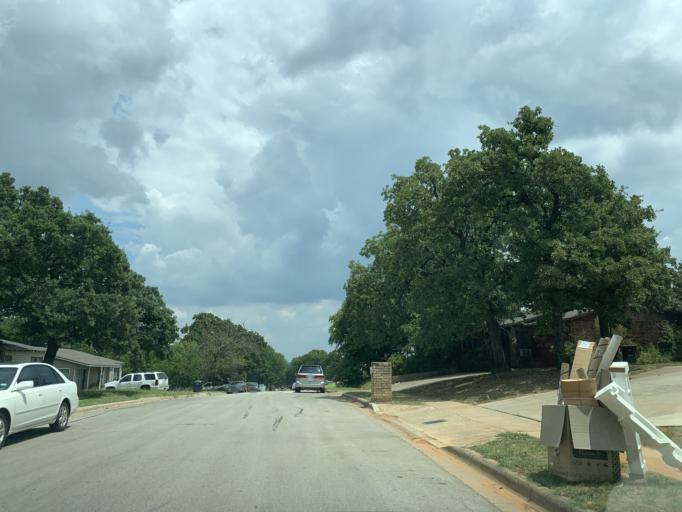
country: US
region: Texas
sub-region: Tarrant County
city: Forest Hill
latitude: 32.7285
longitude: -97.2372
